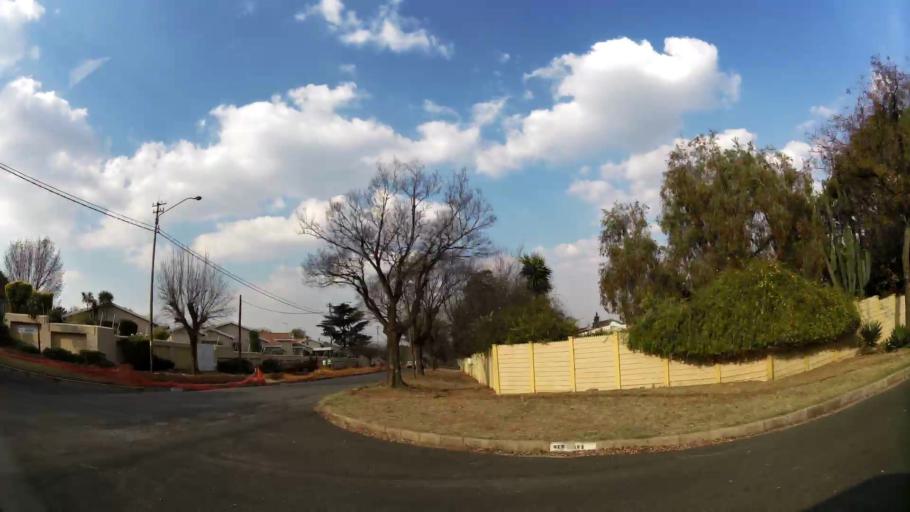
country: ZA
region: Gauteng
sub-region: Ekurhuleni Metropolitan Municipality
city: Germiston
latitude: -26.2459
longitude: 28.1831
